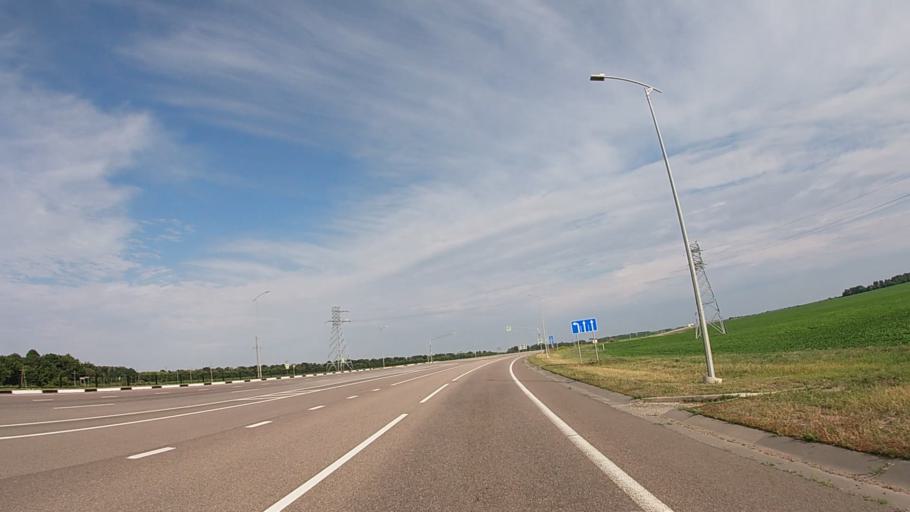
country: RU
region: Belgorod
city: Rakitnoye
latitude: 50.7908
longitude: 35.8678
